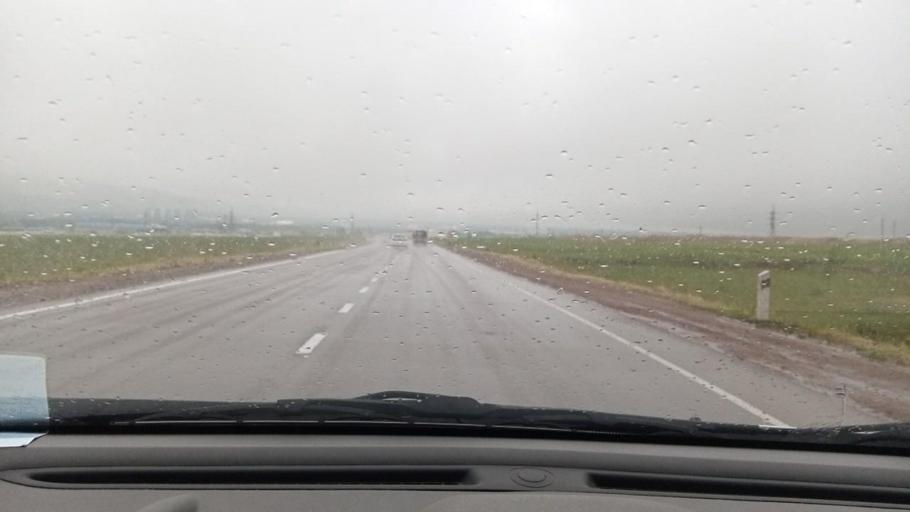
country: UZ
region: Toshkent
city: Angren
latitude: 41.0399
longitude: 70.1461
